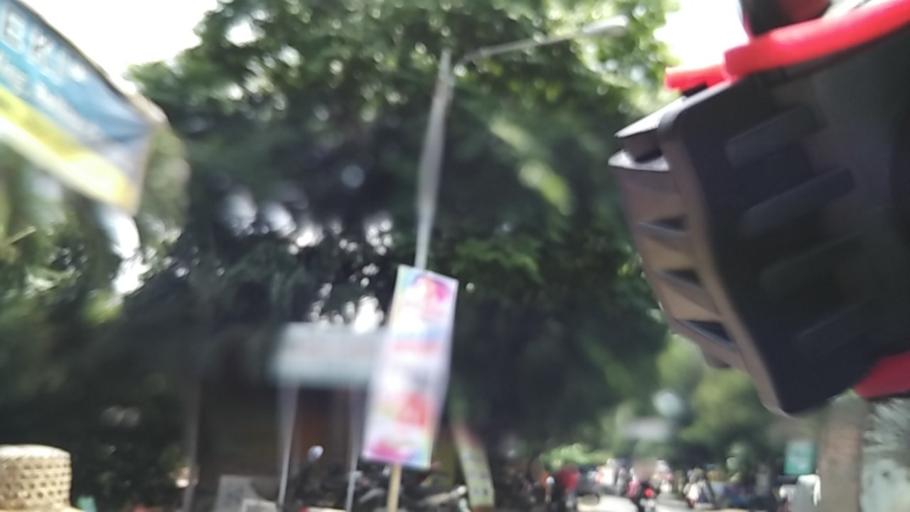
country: ID
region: Central Java
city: Semarang
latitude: -6.9949
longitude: 110.3881
